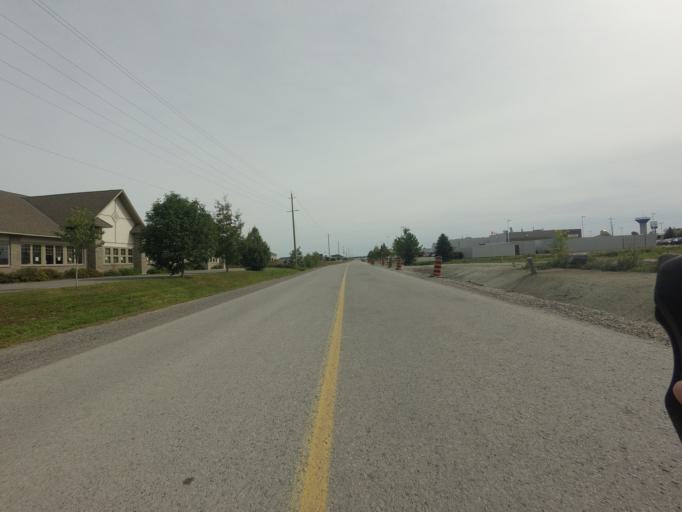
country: CA
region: Ontario
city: Carleton Place
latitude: 45.1429
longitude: -76.1285
